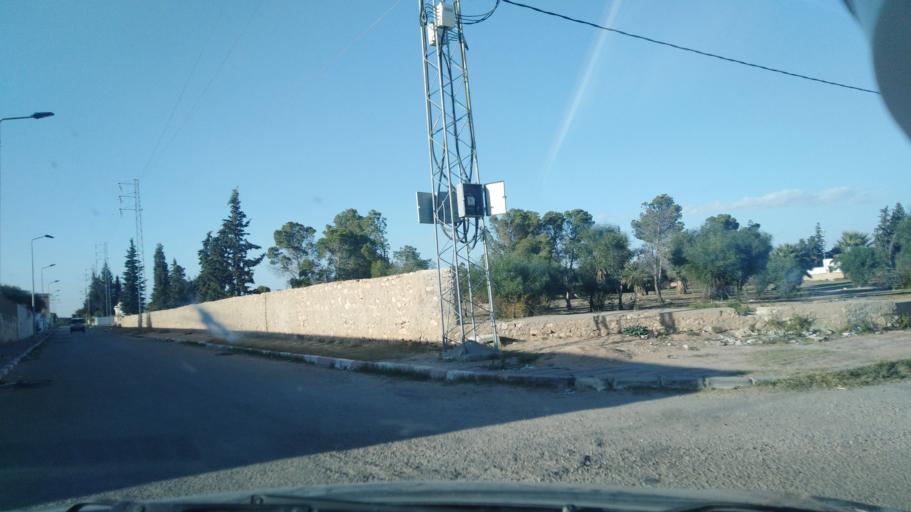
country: TN
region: Al Mahdiyah
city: Shurban
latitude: 34.9642
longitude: 10.3700
